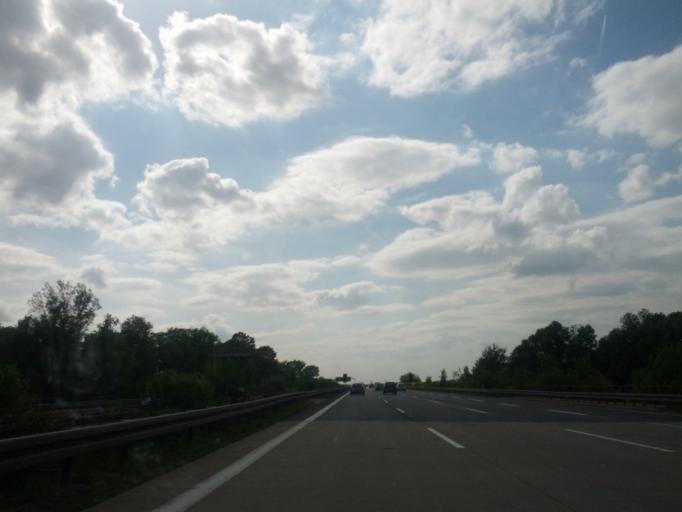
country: DE
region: Saxony
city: Rosswein
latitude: 51.0012
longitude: 13.2017
